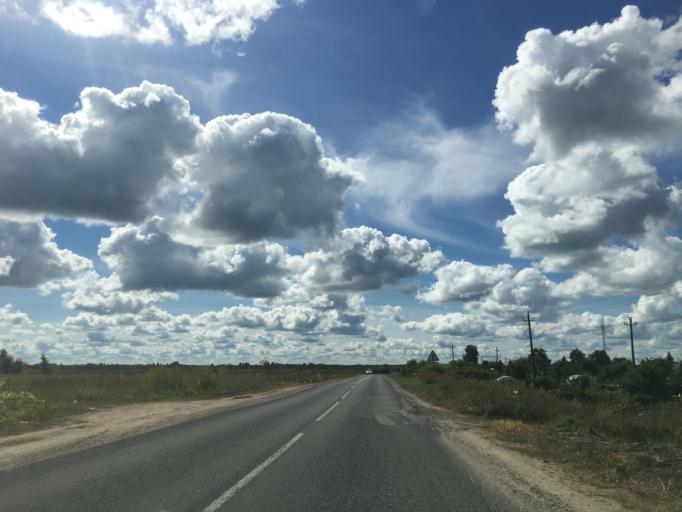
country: RU
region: Pskov
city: Pskov
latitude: 57.7443
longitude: 28.1580
